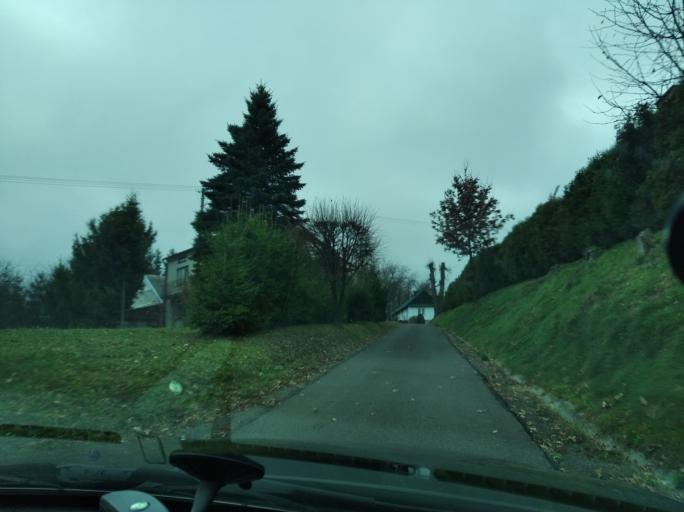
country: PL
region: Subcarpathian Voivodeship
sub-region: Powiat przeworski
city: Jawornik Polski
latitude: 49.8892
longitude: 22.2786
